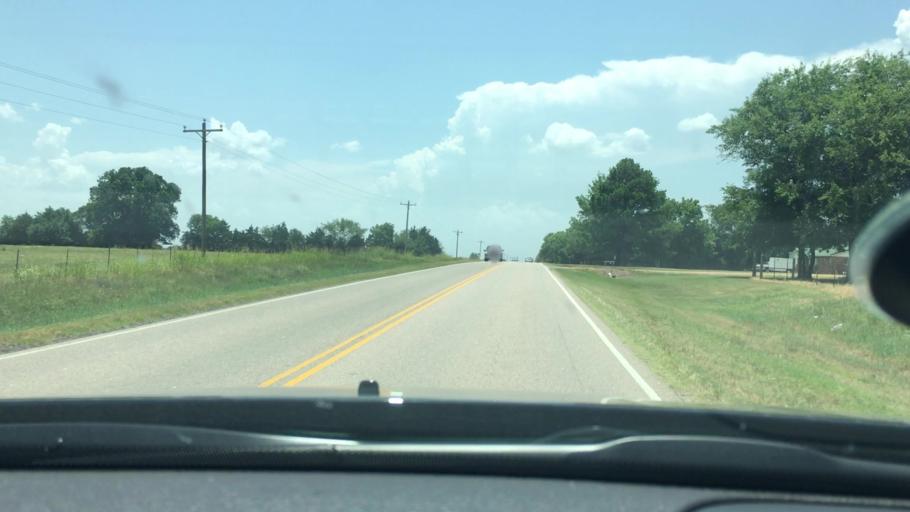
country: US
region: Oklahoma
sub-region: Johnston County
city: Tishomingo
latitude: 34.2909
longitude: -96.6711
